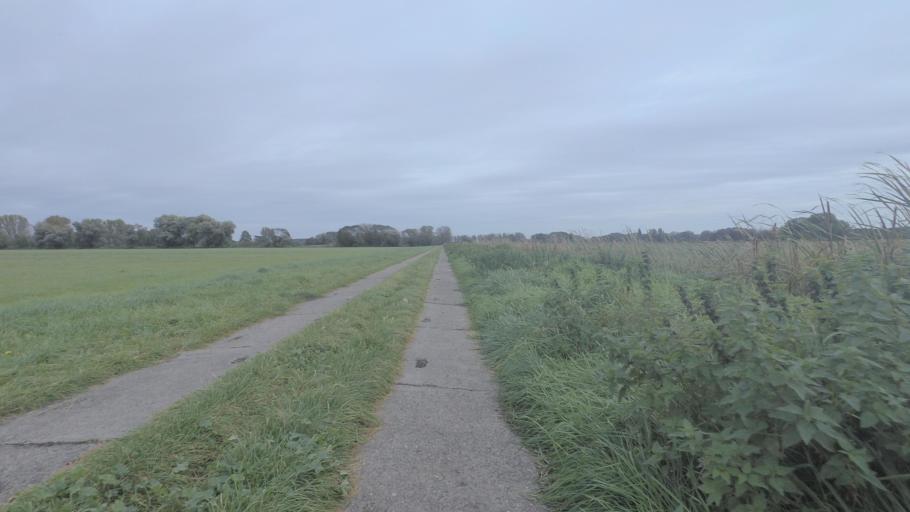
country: DE
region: Brandenburg
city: Grossbeeren
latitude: 52.2882
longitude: 13.3410
